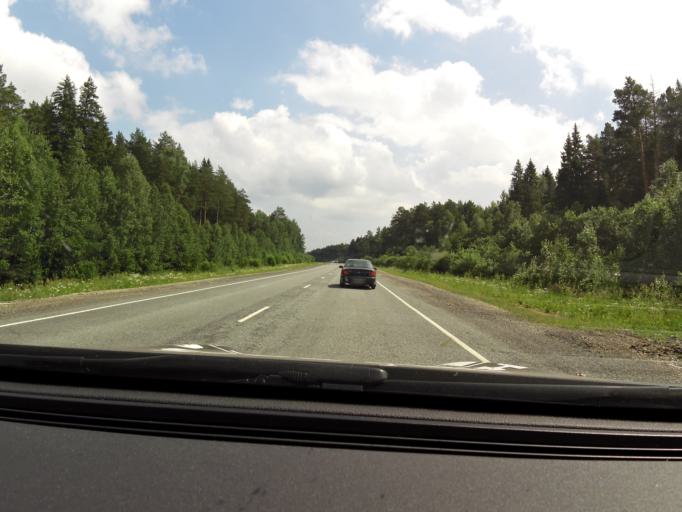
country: RU
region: Sverdlovsk
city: Achit
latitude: 56.8038
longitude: 57.8420
